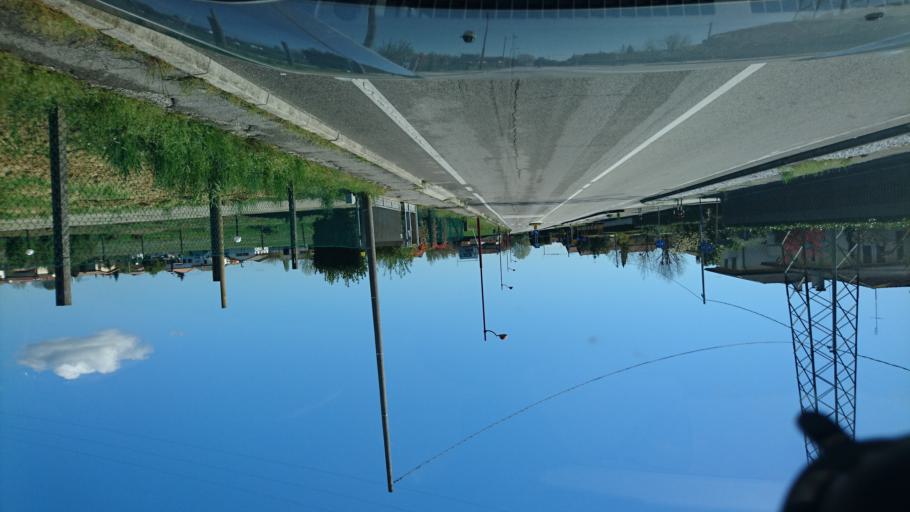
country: IT
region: Veneto
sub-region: Provincia di Padova
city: Mejaniga
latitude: 45.4669
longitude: 11.9035
